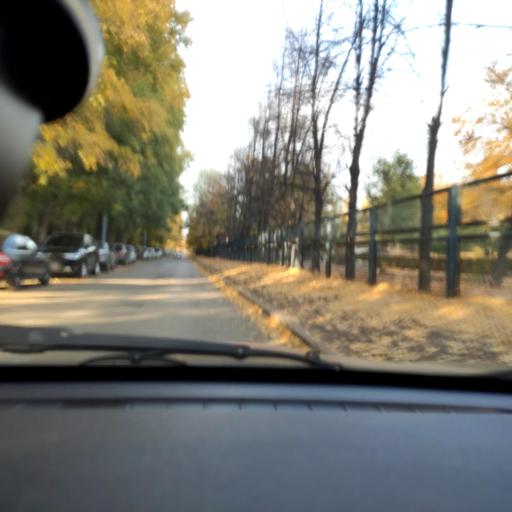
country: RU
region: Samara
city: Tol'yatti
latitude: 53.5167
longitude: 49.2661
